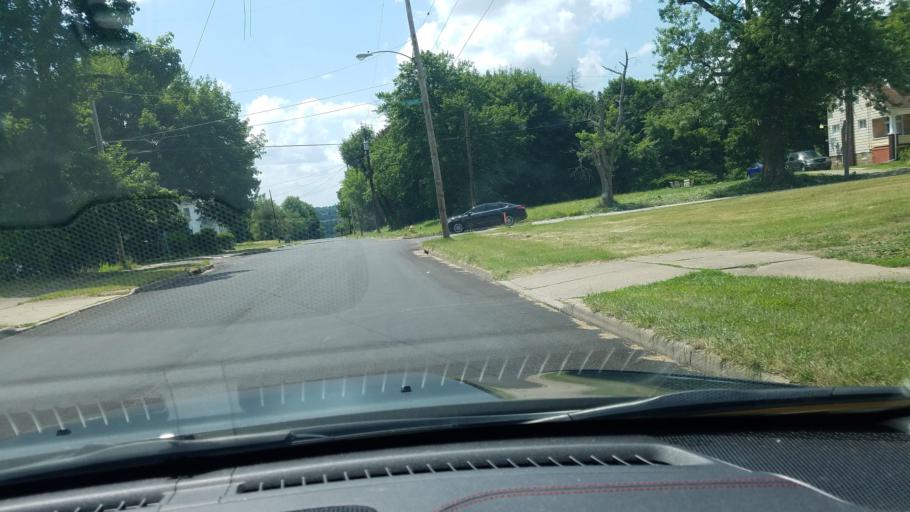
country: US
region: Ohio
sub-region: Mahoning County
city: Youngstown
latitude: 41.0947
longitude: -80.6279
